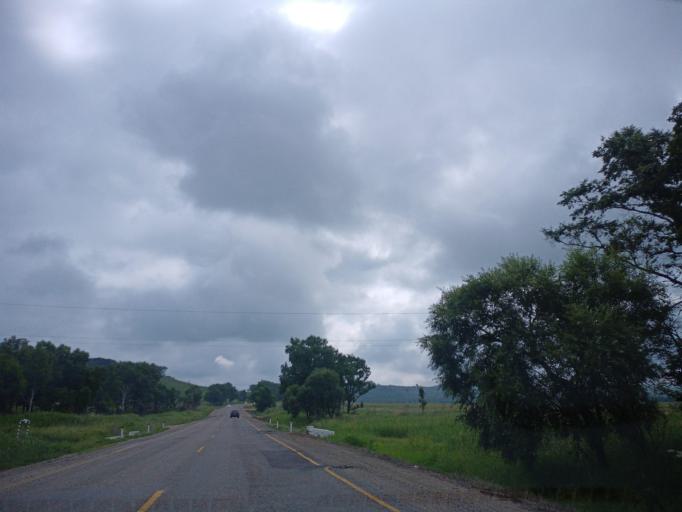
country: RU
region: Primorskiy
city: Dal'nerechensk
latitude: 46.0382
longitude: 133.8782
